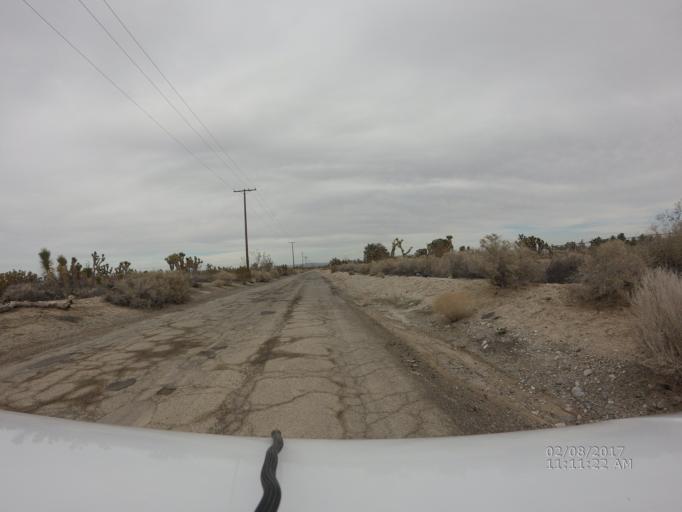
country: US
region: California
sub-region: San Bernardino County
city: Pinon Hills
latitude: 34.4782
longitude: -117.6599
